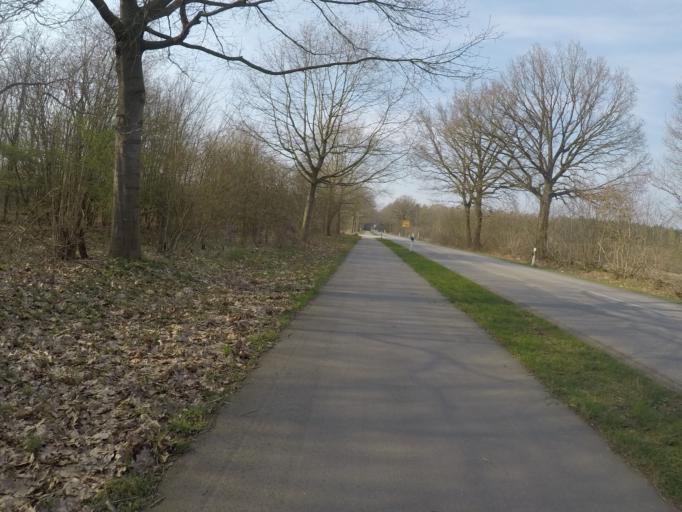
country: DE
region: Schleswig-Holstein
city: Wittenborn
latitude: 53.9426
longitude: 10.2219
